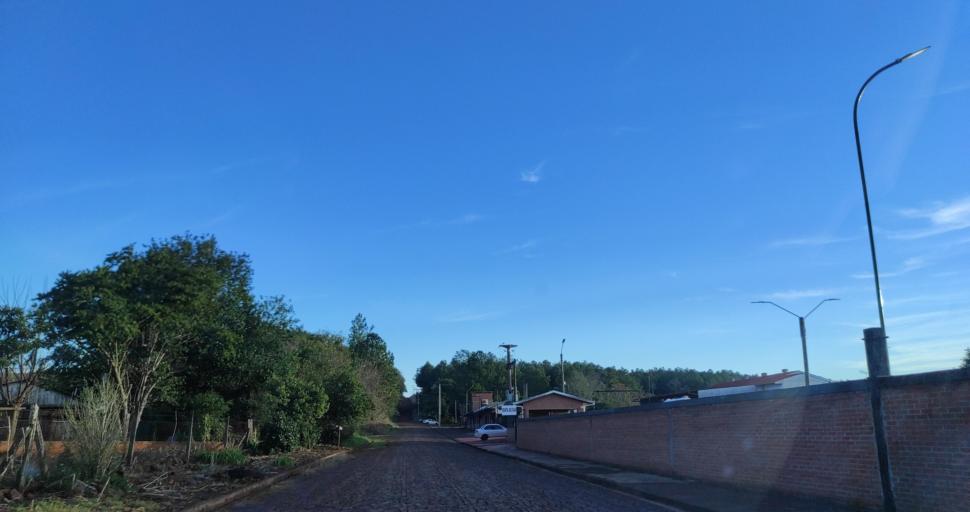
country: AR
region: Misiones
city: Capiovi
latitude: -26.8632
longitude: -55.0474
